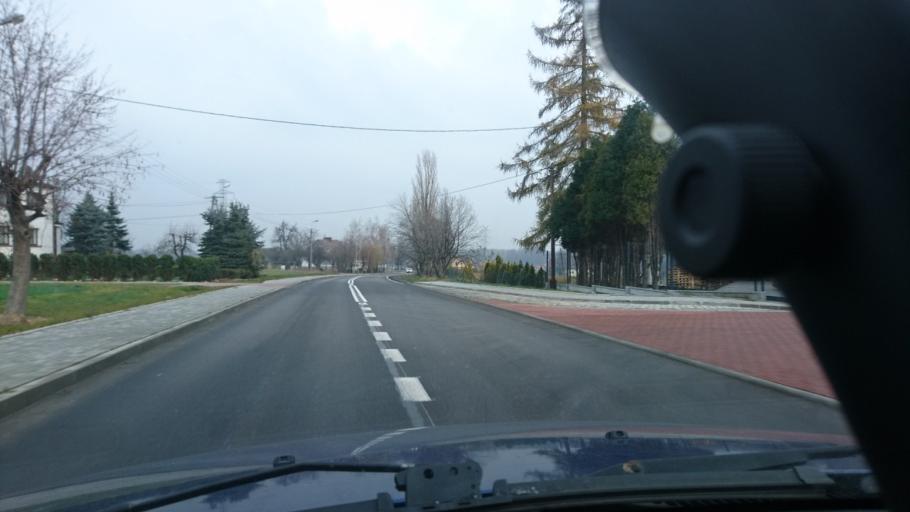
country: PL
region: Silesian Voivodeship
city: Janowice
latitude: 49.8617
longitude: 19.1143
